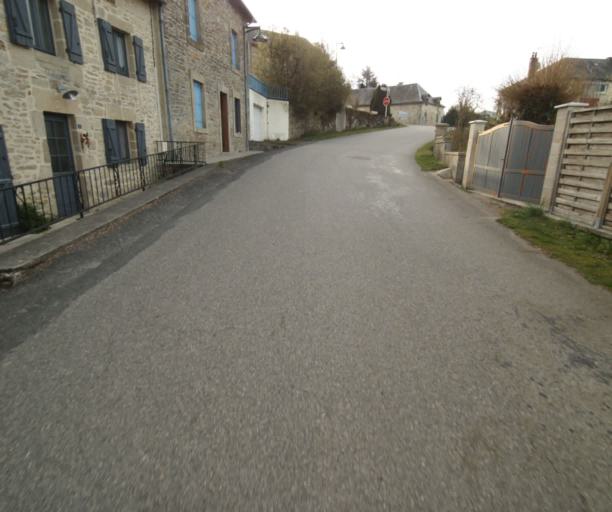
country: FR
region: Limousin
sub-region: Departement de la Correze
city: Treignac
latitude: 45.4744
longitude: 1.7910
